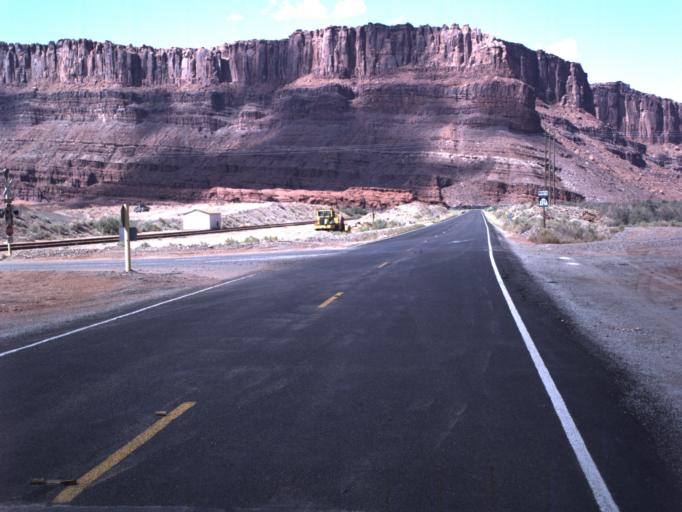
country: US
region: Utah
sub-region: Grand County
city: Moab
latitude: 38.5238
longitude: -109.6542
